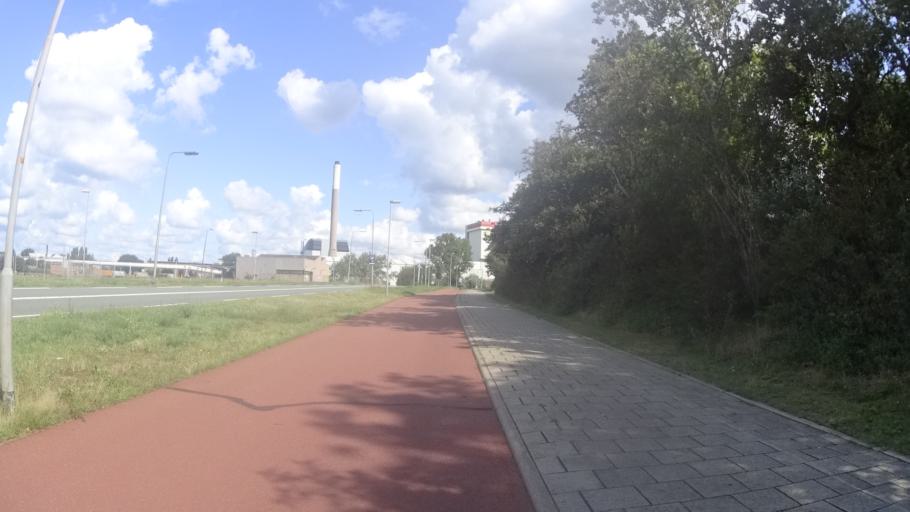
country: NL
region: North Holland
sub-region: Gemeente Velsen
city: Velsen-Zuid
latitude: 52.4668
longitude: 4.6328
